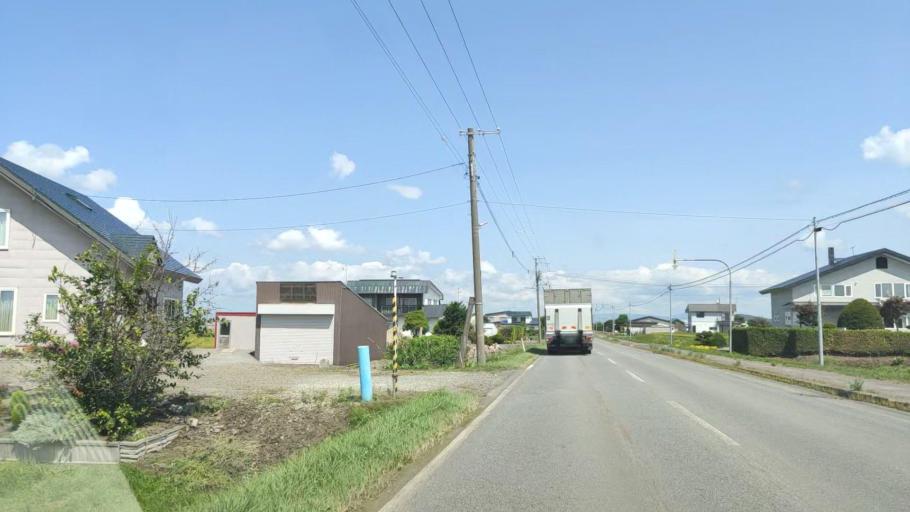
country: JP
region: Hokkaido
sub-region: Asahikawa-shi
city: Asahikawa
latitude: 43.7195
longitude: 142.4577
